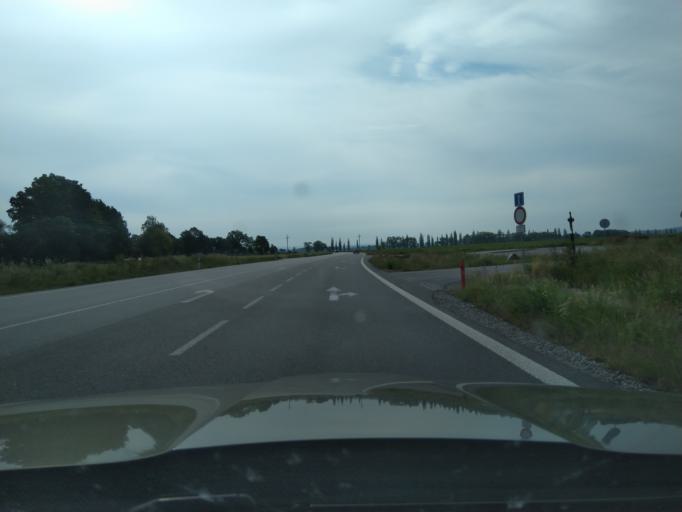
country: CZ
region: Jihocesky
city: Netolice
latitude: 49.0315
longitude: 14.2613
